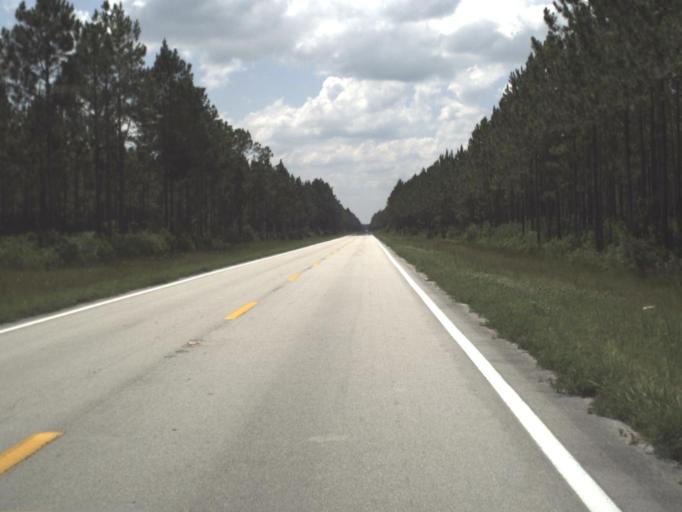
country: US
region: Florida
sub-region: Baker County
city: Macclenny
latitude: 30.5550
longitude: -82.3707
